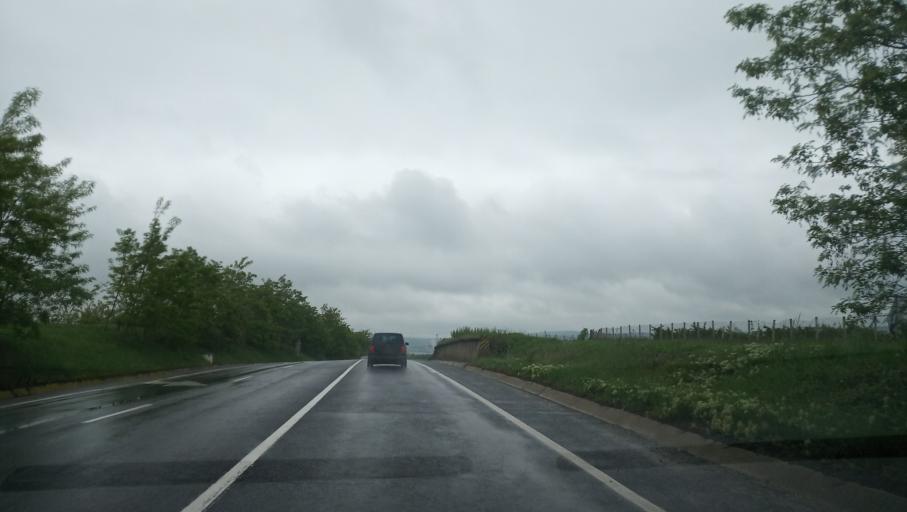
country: RO
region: Sibiu
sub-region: Oras Miercurea Sibiului
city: Miercurea Sibiului
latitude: 45.8683
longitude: 23.8066
